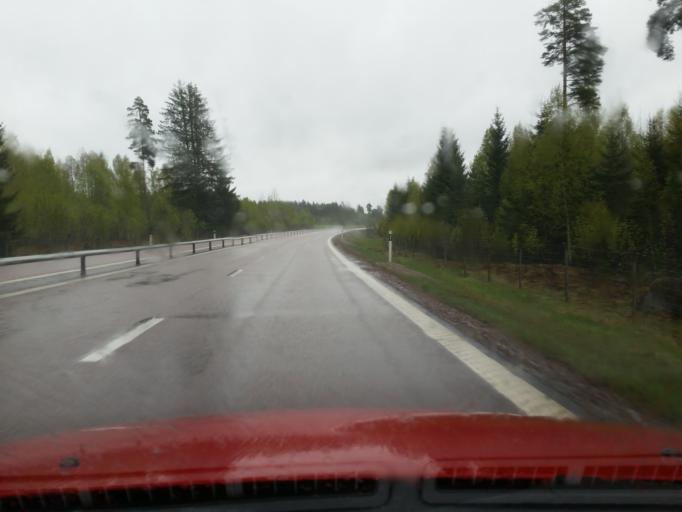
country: SE
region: Dalarna
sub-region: Hedemora Kommun
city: Hedemora
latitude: 60.3251
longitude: 15.8758
